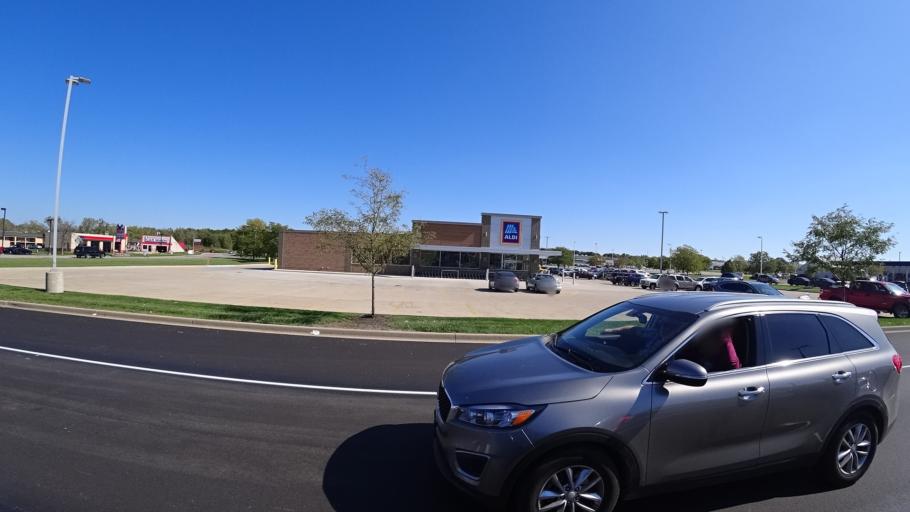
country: US
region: Indiana
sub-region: LaPorte County
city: Michigan City
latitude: 41.6756
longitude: -86.8939
